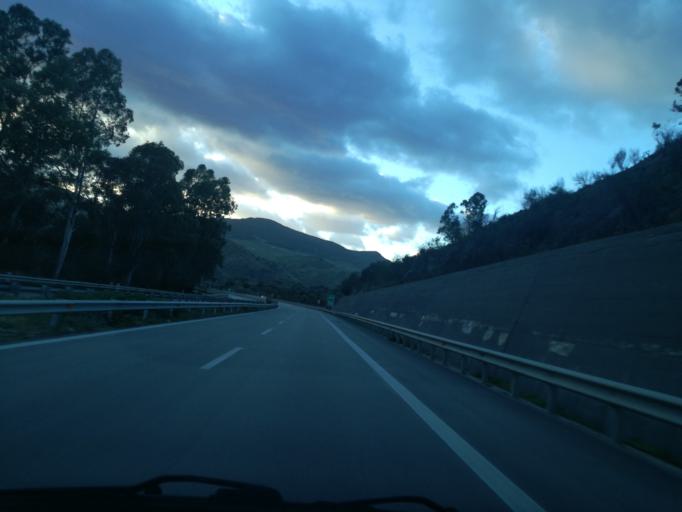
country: IT
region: Sicily
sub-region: Palermo
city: Scillato
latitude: 37.8637
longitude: 13.8856
